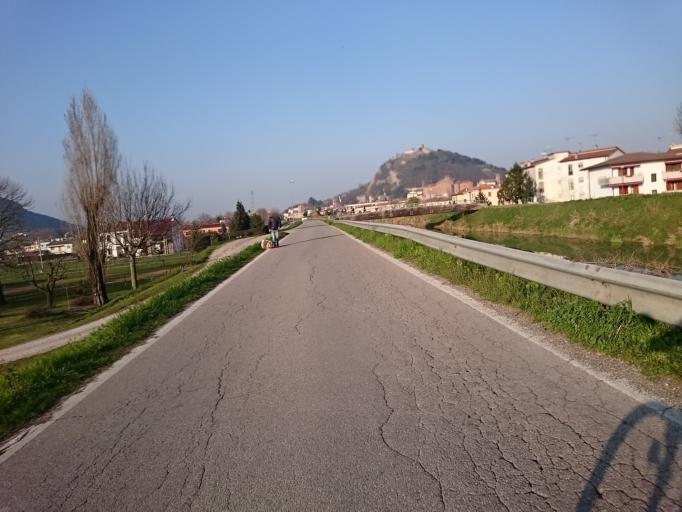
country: IT
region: Veneto
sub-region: Provincia di Padova
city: Monselice
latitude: 45.2349
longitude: 11.7433
